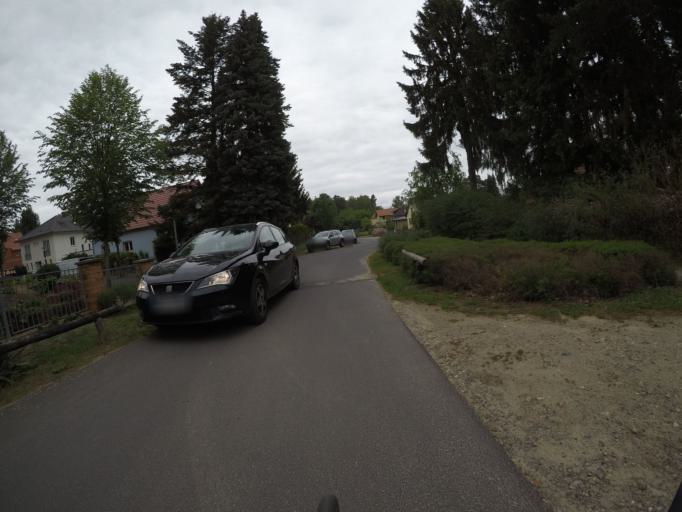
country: DE
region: Brandenburg
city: Glienicke
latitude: 52.6415
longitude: 13.3173
